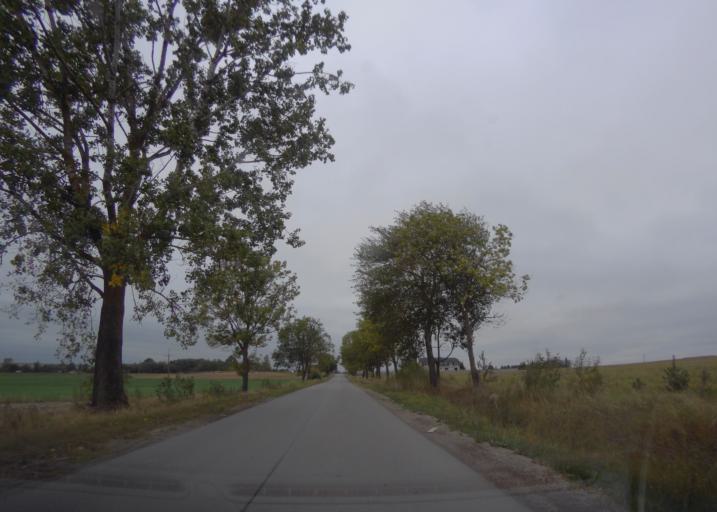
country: PL
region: Lublin Voivodeship
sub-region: Powiat chelmski
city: Sawin
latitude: 51.2139
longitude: 23.4390
